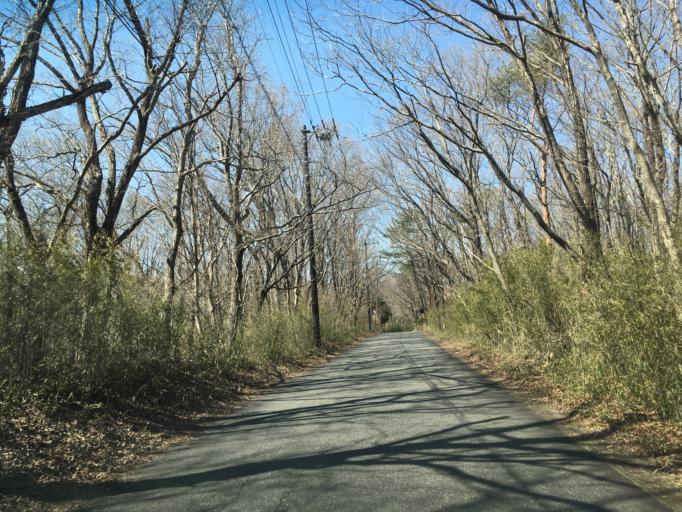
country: JP
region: Tochigi
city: Kuroiso
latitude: 37.0704
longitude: 140.0037
